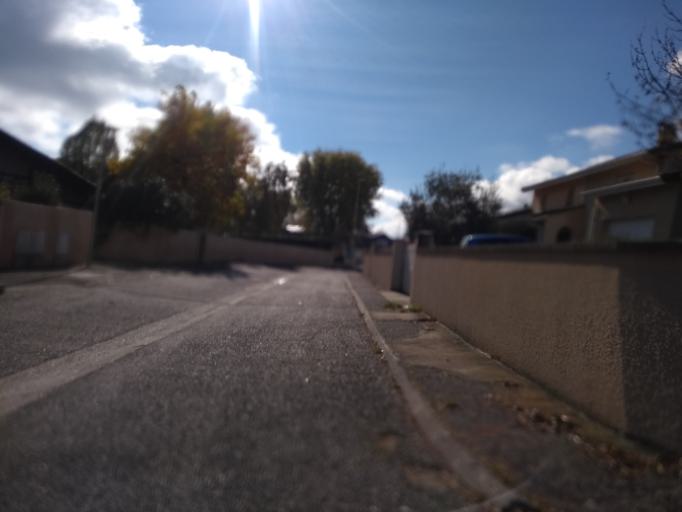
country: FR
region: Aquitaine
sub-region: Departement de la Gironde
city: Canejan
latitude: 44.7726
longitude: -0.6300
